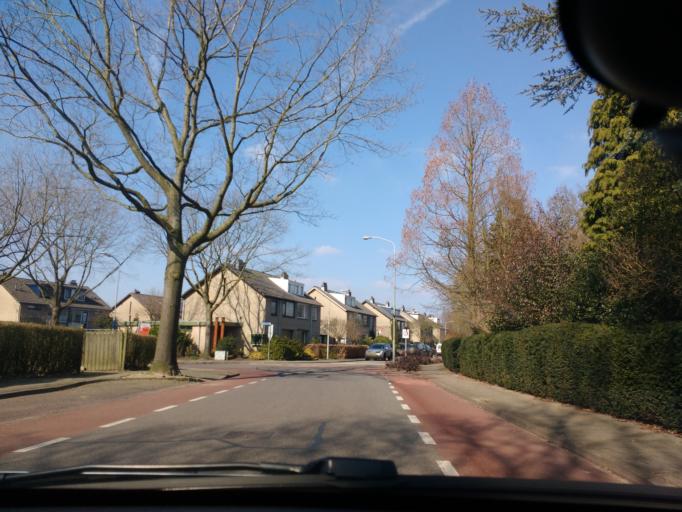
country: NL
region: Gelderland
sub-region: Gemeente Nijmegen
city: Nijmegen
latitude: 51.7875
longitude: 5.8567
